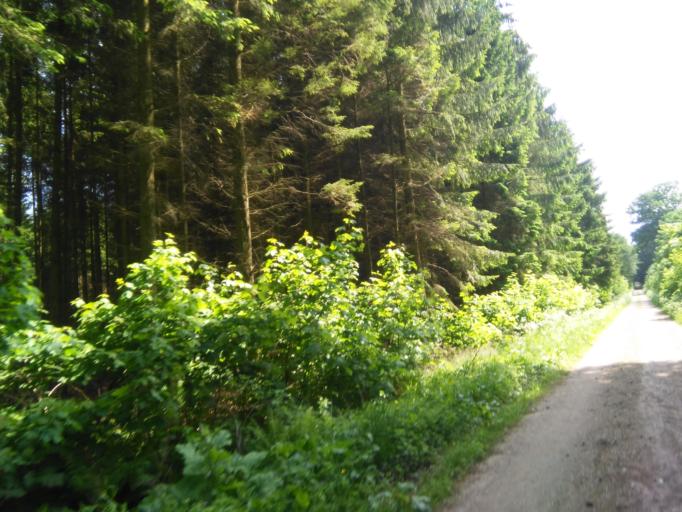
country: DK
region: Central Jutland
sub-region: Favrskov Kommune
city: Hinnerup
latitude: 56.2638
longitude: 10.0431
